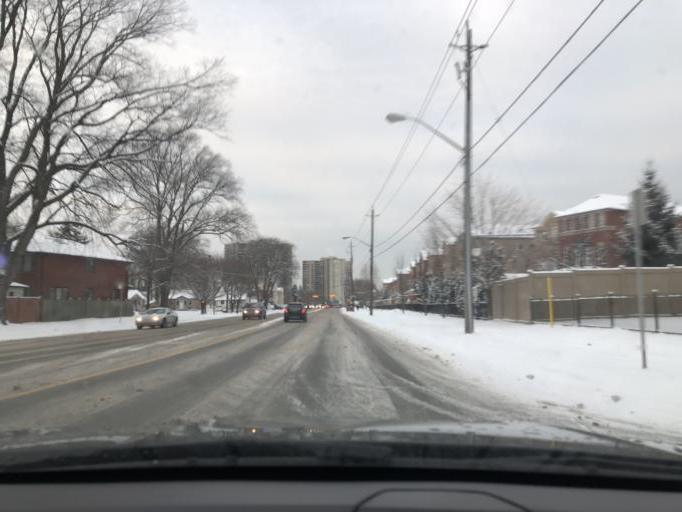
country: CA
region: Ontario
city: Toronto
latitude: 43.6971
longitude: -79.4966
